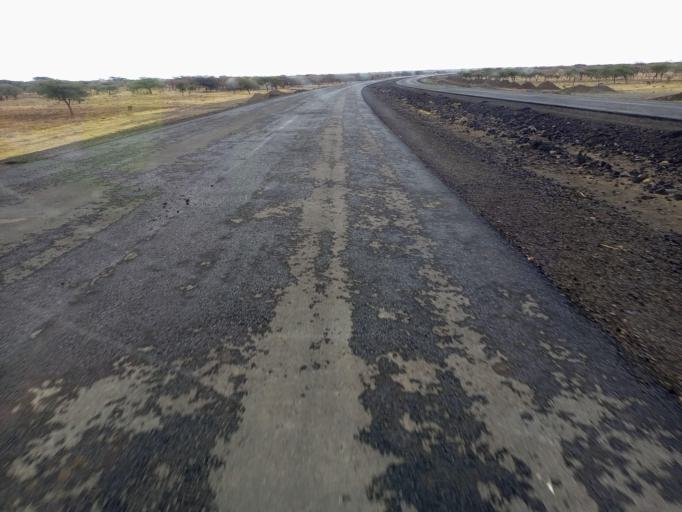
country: ET
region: Oromiya
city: Ziway
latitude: 7.6718
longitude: 38.6814
